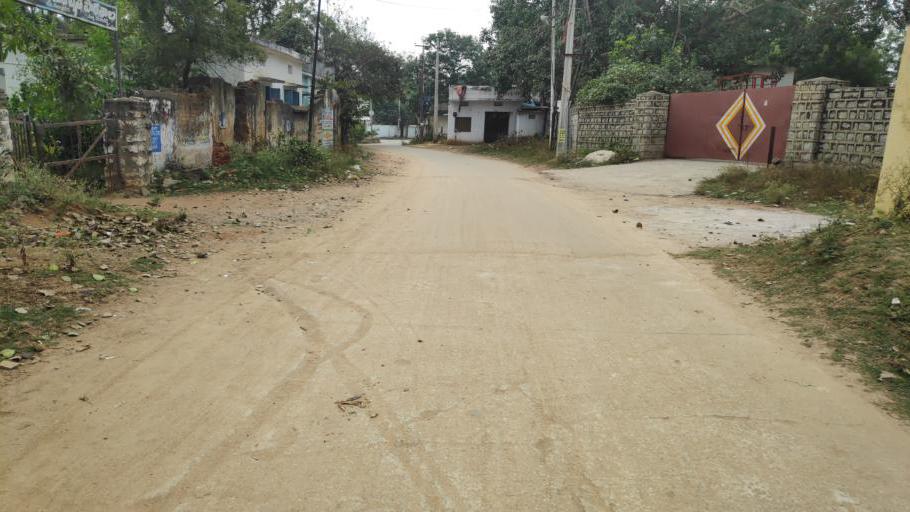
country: IN
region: Telangana
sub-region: Rangareddi
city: Secunderabad
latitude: 17.5331
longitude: 78.5159
